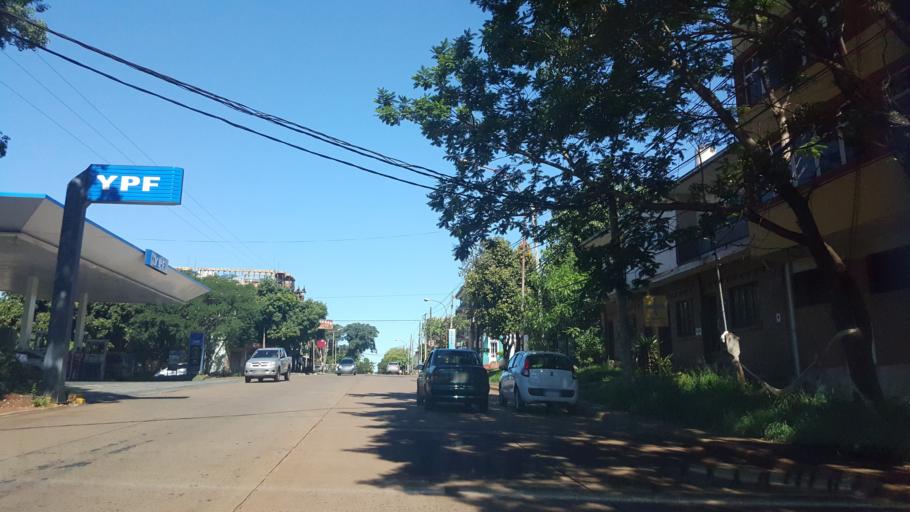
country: AR
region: Misiones
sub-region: Departamento de Capital
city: Posadas
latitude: -27.3728
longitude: -55.9124
